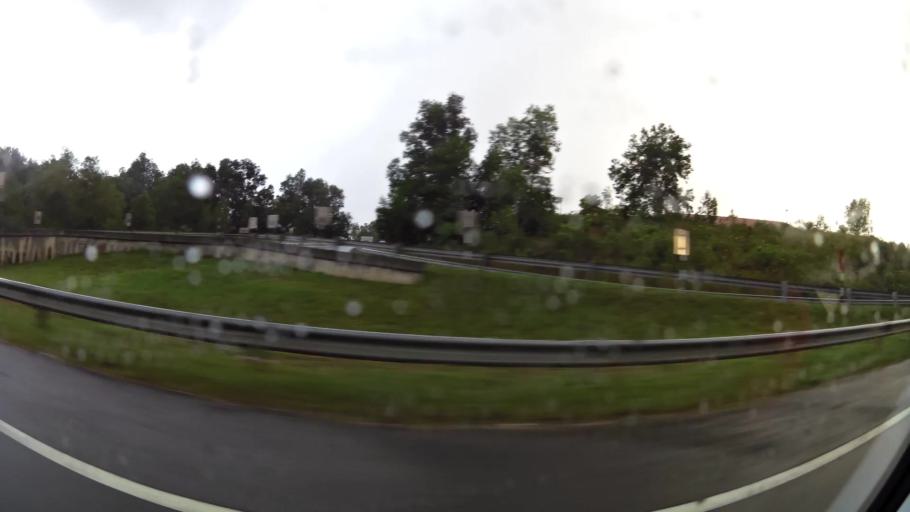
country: BN
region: Brunei and Muara
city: Bandar Seri Begawan
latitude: 4.9264
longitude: 114.9630
